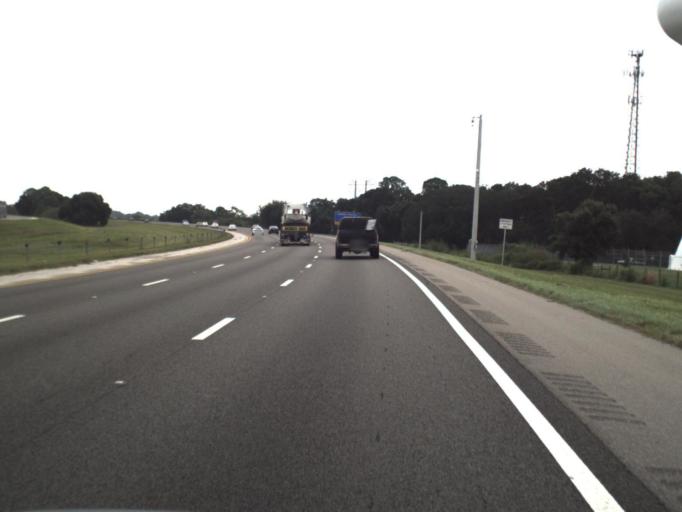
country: US
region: Florida
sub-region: Manatee County
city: Ellenton
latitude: 27.5110
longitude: -82.5004
